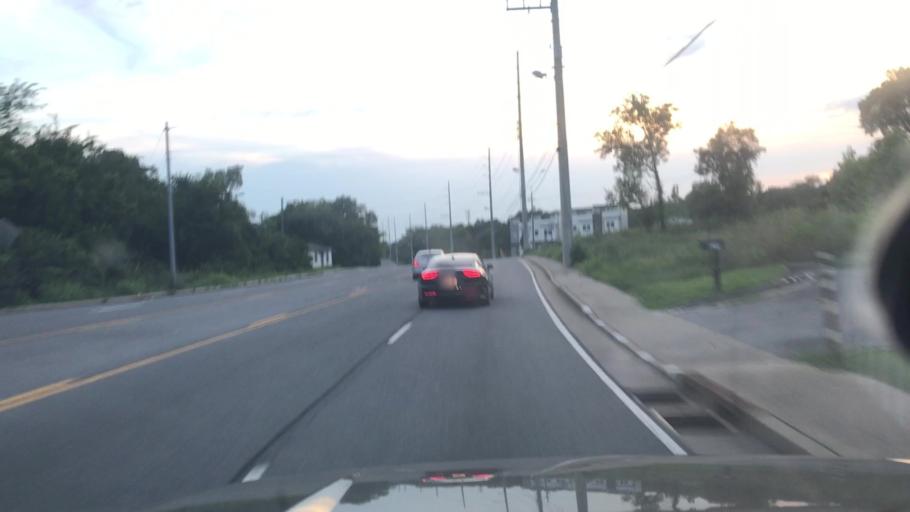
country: US
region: Tennessee
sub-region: Davidson County
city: Nashville
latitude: 36.2068
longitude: -86.7938
